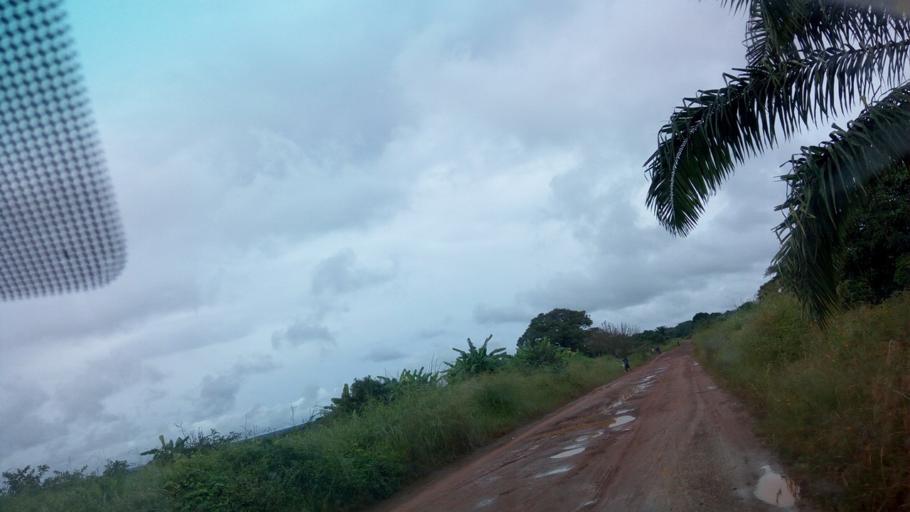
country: ZM
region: Luapula
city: Nchelenge
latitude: -9.1377
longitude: 28.2959
